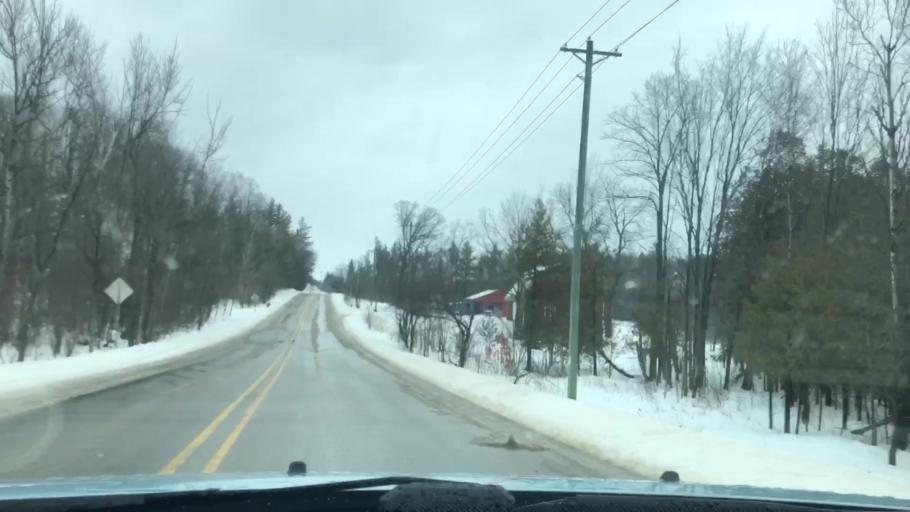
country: US
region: Michigan
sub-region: Charlevoix County
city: East Jordan
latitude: 45.1064
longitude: -85.1284
